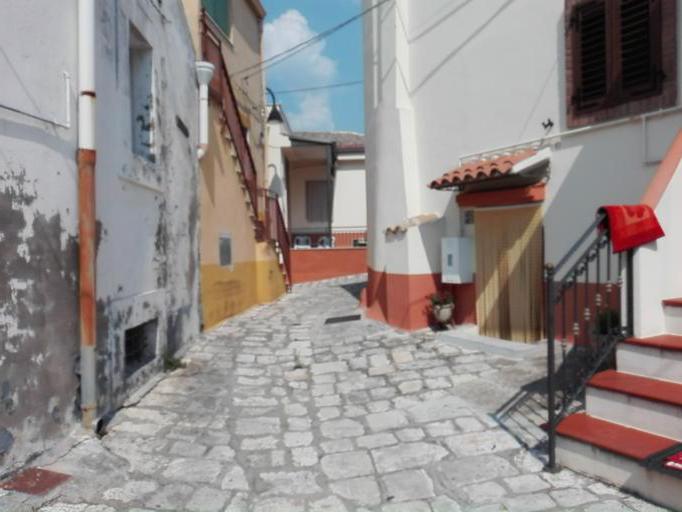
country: IT
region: Basilicate
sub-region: Provincia di Matera
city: Miglionico
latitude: 40.5706
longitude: 16.4997
